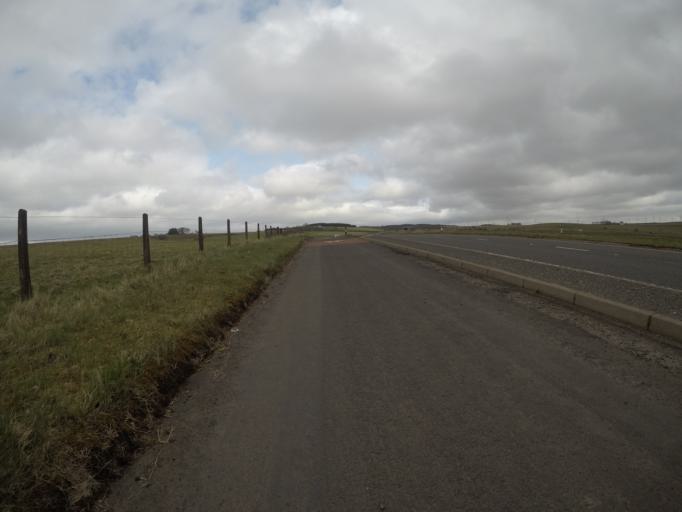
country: GB
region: Scotland
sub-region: East Ayrshire
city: Galston
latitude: 55.6883
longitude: -4.4120
